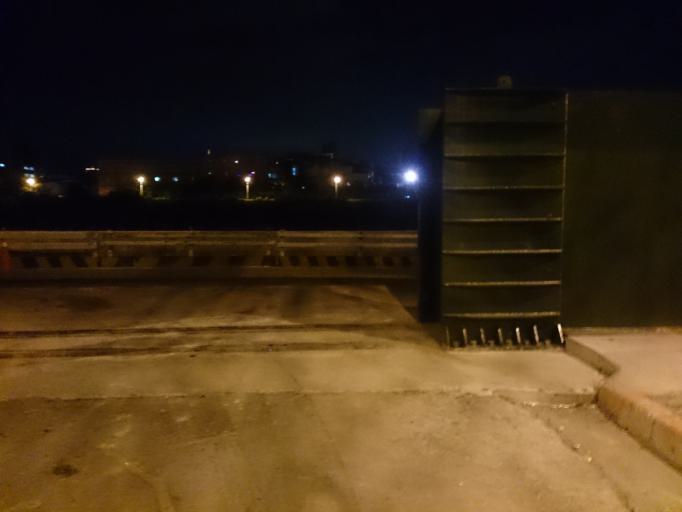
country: TW
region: Taipei
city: Taipei
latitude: 25.0591
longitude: 121.6214
